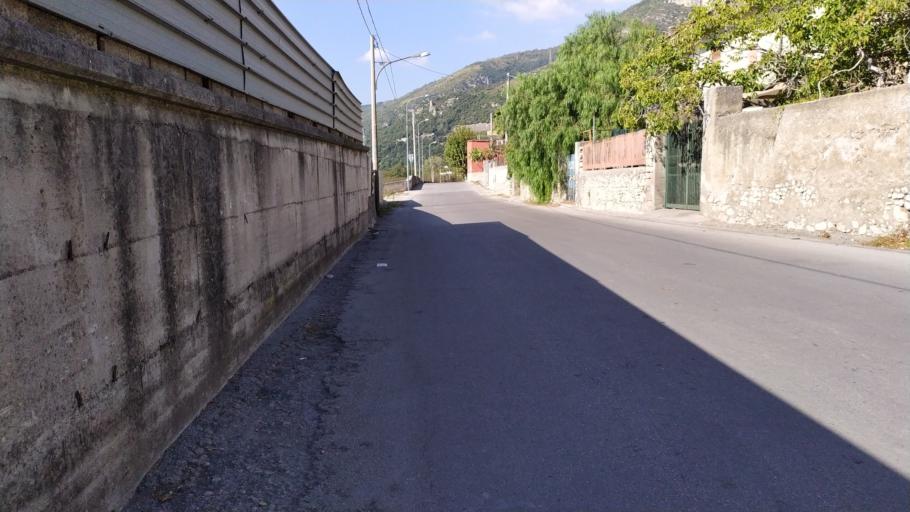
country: IT
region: Campania
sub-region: Provincia di Salerno
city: Sarno
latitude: 40.8256
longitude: 14.6023
